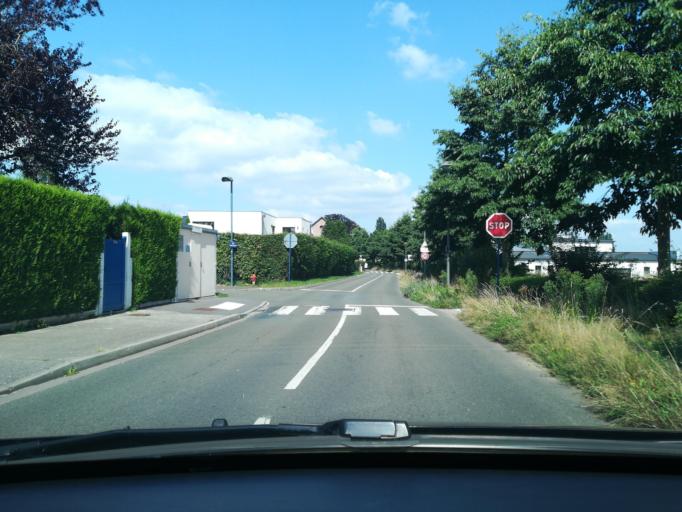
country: FR
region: Haute-Normandie
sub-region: Departement de la Seine-Maritime
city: Bois-Guillaume
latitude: 49.4634
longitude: 1.1244
